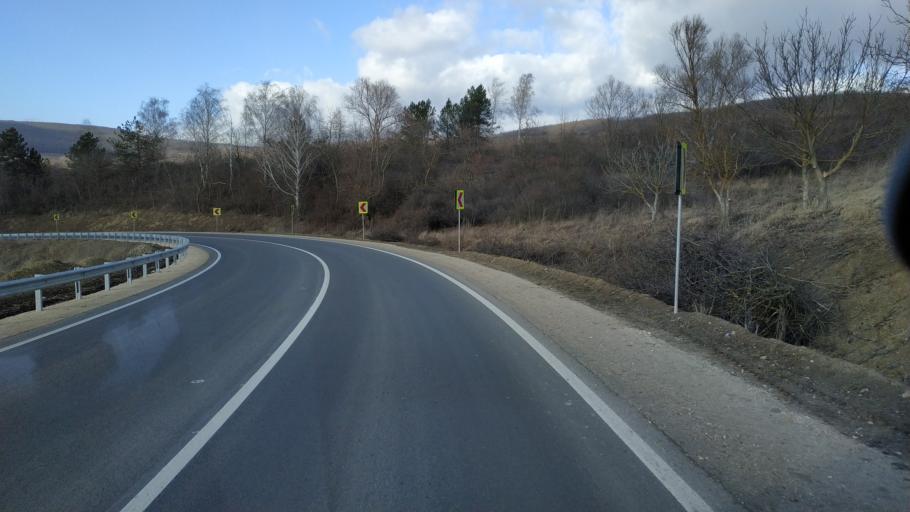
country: MD
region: Calarasi
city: Calarasi
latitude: 47.2988
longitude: 28.1530
